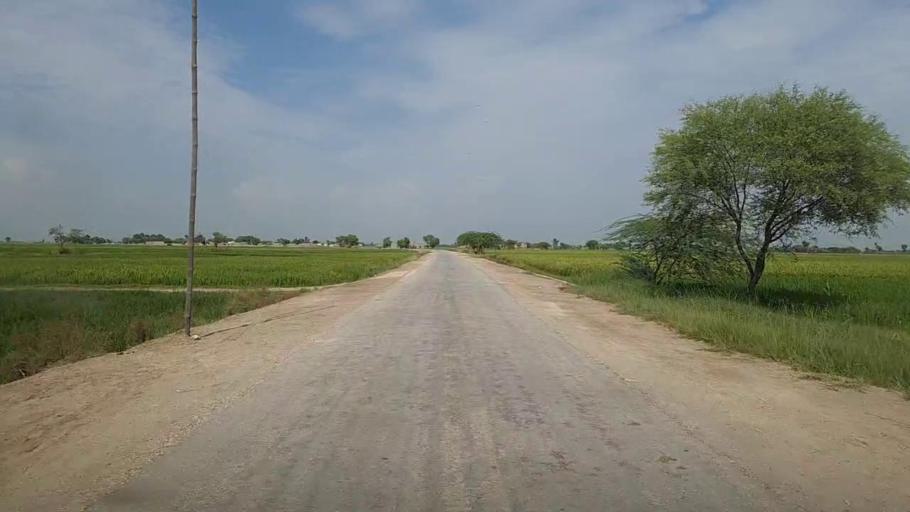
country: PK
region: Sindh
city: Thul
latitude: 28.2614
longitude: 68.8140
